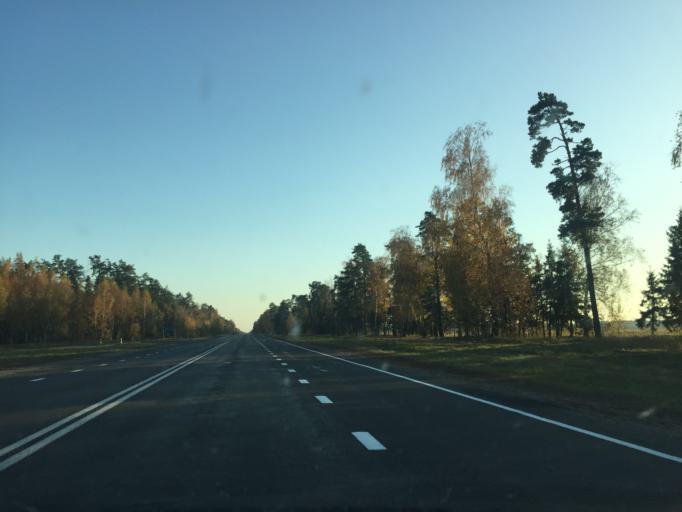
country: BY
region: Mogilev
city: Poselok Voskhod
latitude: 53.7314
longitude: 30.3667
